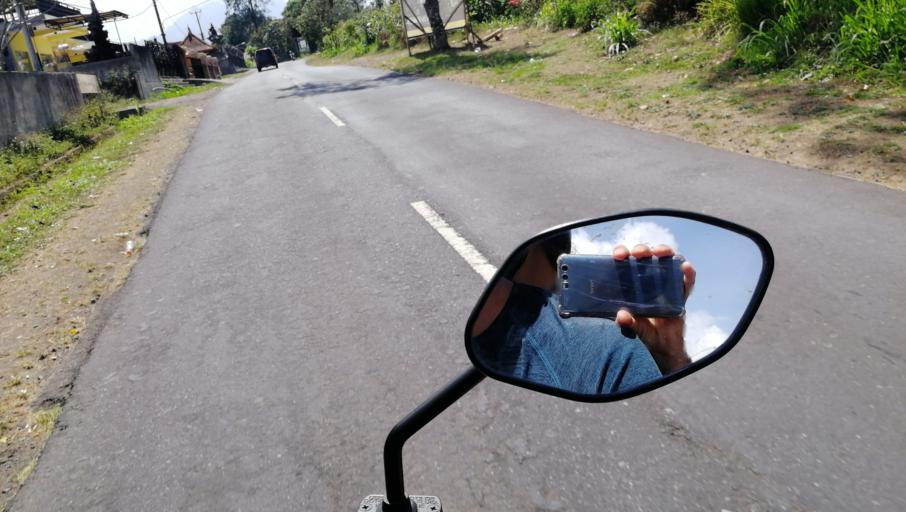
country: ID
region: Bali
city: Munduk
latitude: -8.2378
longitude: 115.1176
